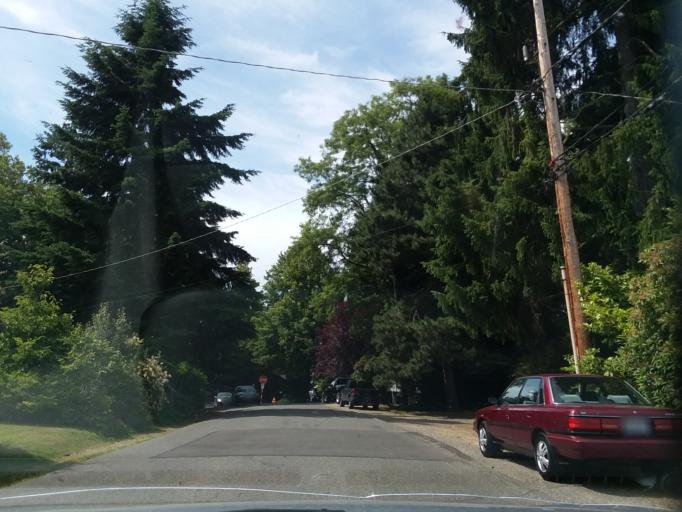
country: US
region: Washington
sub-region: King County
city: Shoreline
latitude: 47.7237
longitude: -122.3119
